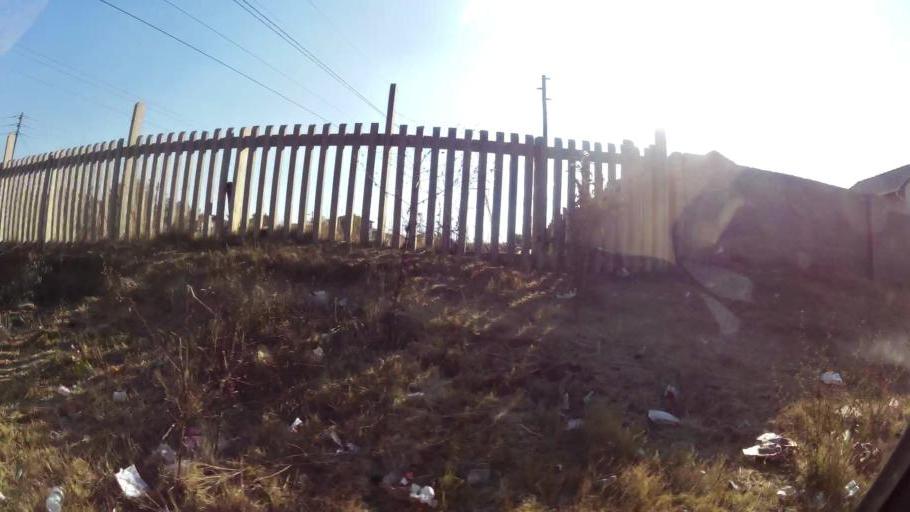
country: ZA
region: Gauteng
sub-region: West Rand District Municipality
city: Muldersdriseloop
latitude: -26.0371
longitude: 27.9146
